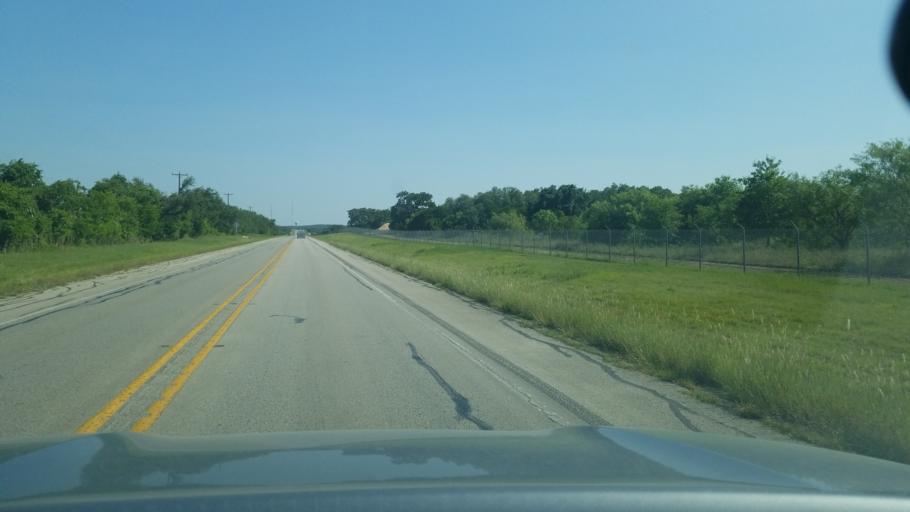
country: US
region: Texas
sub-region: Bexar County
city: Timberwood Park
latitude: 29.7357
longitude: -98.5130
